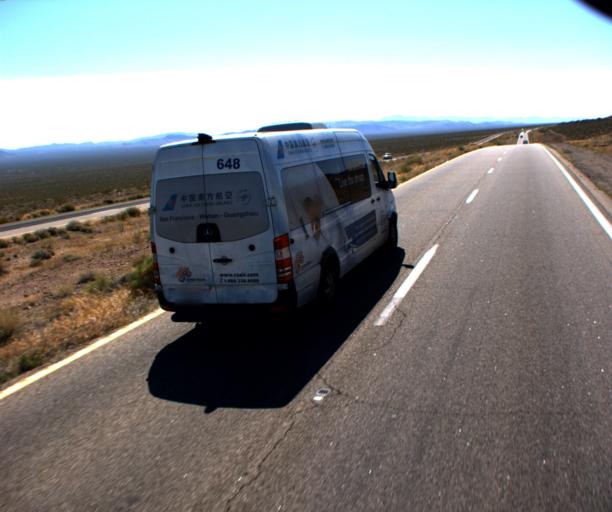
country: US
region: Arizona
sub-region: Mohave County
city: Dolan Springs
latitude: 35.7930
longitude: -114.5286
